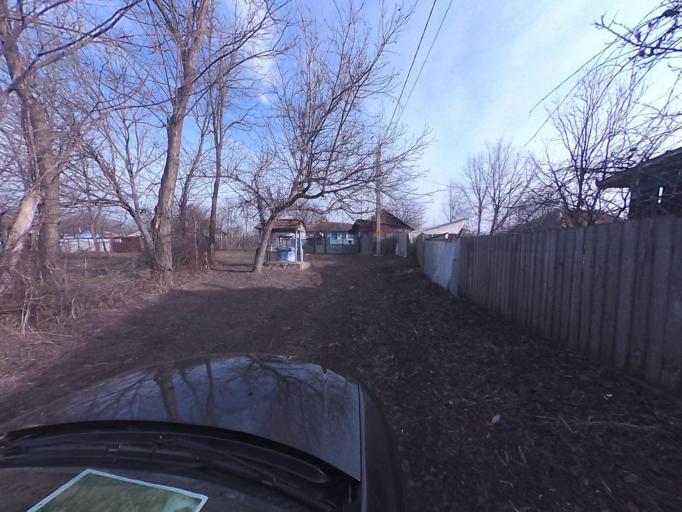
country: RO
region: Vaslui
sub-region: Comuna Solesti
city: Solesti
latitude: 46.8124
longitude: 27.7685
